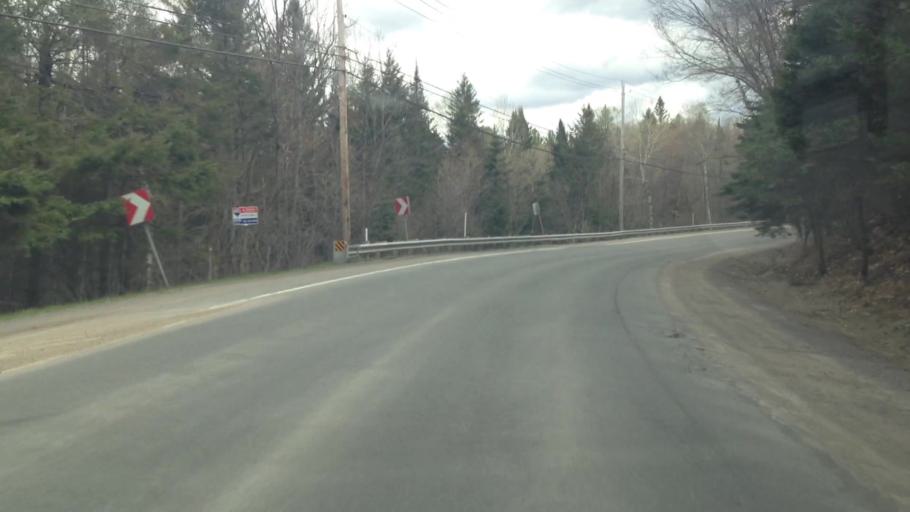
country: CA
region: Quebec
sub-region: Laurentides
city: Sainte-Adele
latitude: 45.9729
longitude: -74.1148
